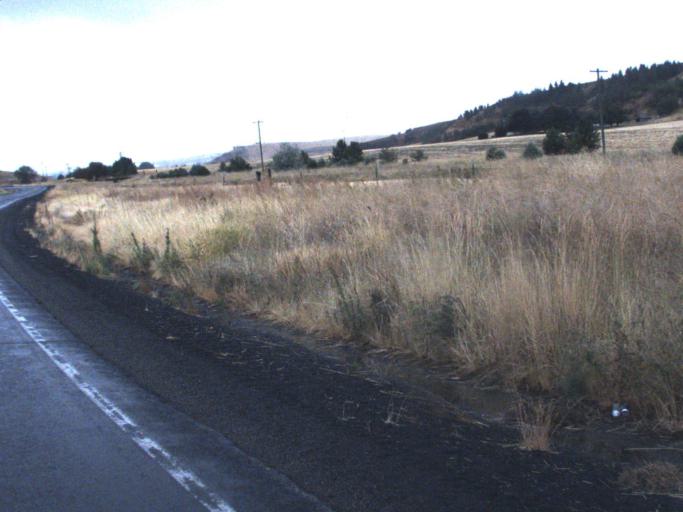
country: US
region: Washington
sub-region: Whitman County
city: Colfax
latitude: 47.1061
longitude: -117.6240
